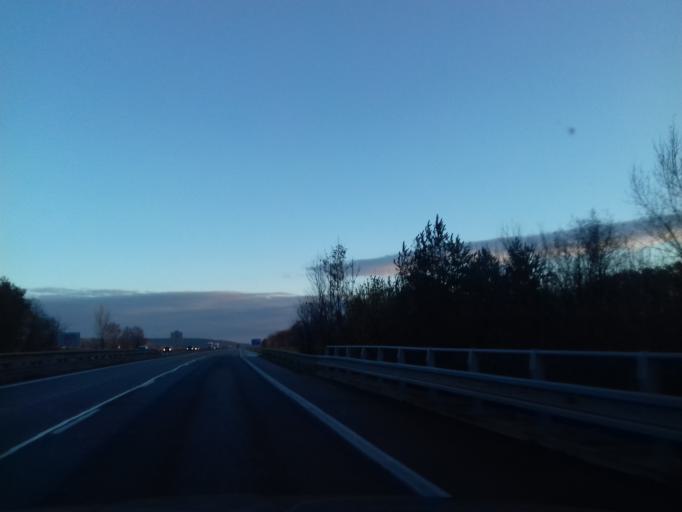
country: CZ
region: South Moravian
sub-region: Okres Vyskov
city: Vyskov
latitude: 49.2876
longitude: 17.0201
